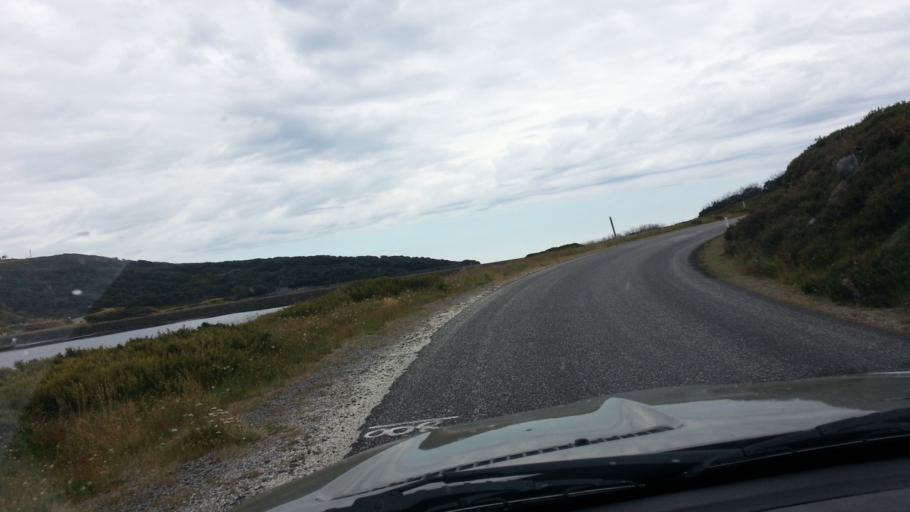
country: AU
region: Victoria
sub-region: Alpine
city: Mount Beauty
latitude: -36.8750
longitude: 147.2992
